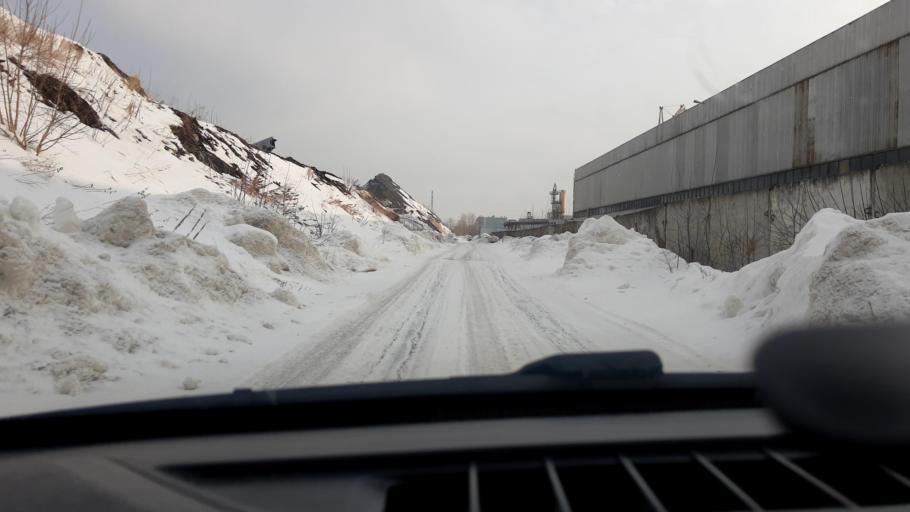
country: RU
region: Nizjnij Novgorod
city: Nizhniy Novgorod
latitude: 56.2377
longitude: 43.9138
